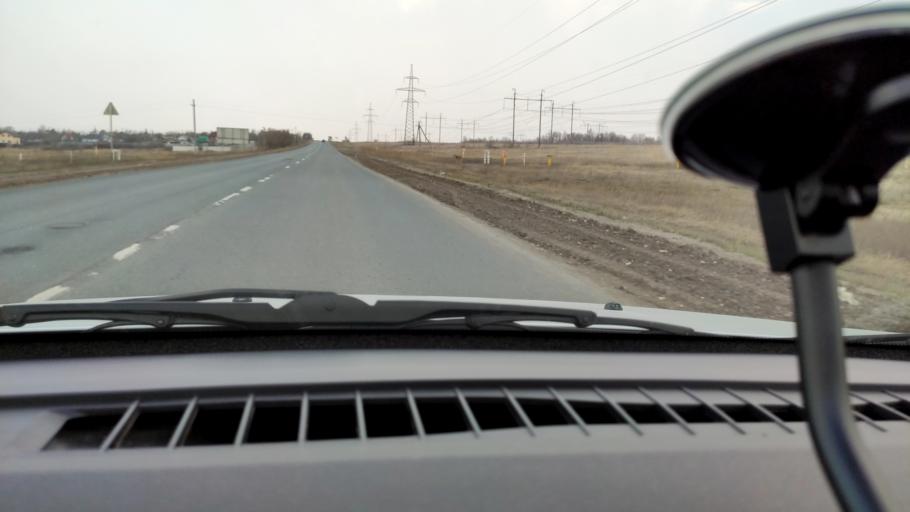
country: RU
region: Samara
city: Dubovyy Umet
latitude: 53.0656
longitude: 50.3785
